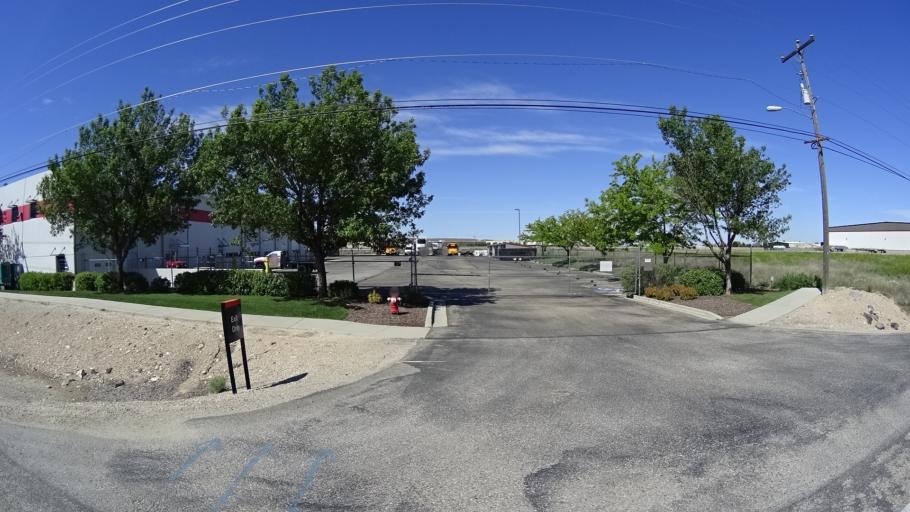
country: US
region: Idaho
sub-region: Ada County
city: Boise
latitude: 43.5215
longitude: -116.1470
